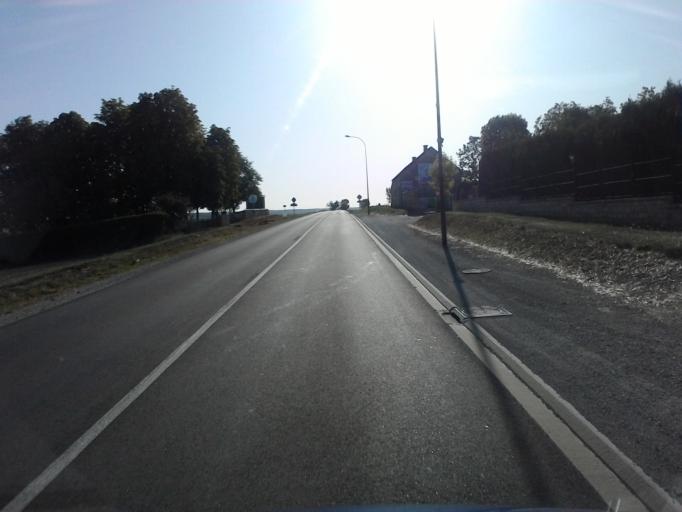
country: FR
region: Champagne-Ardenne
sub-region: Departement de l'Aube
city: Bar-sur-Seine
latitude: 48.1378
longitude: 4.3161
